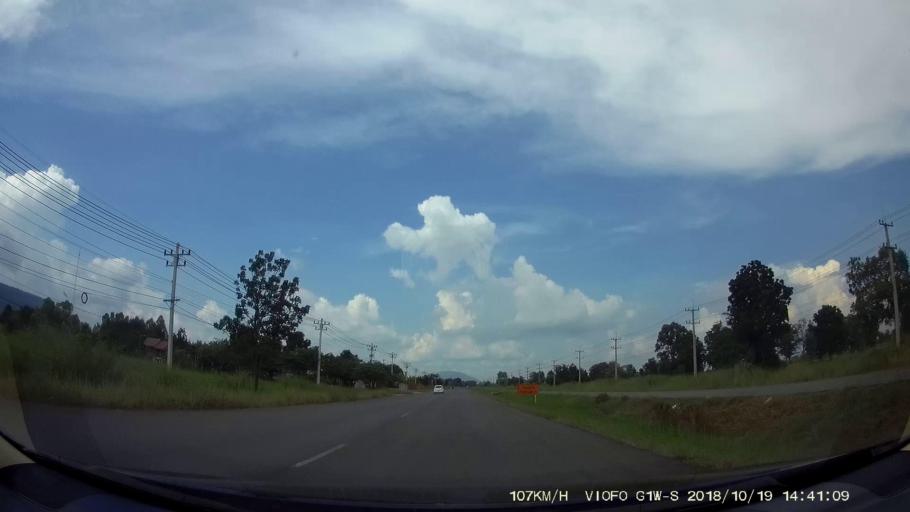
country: TH
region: Chaiyaphum
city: Phu Khiao
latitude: 16.2524
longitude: 102.1982
